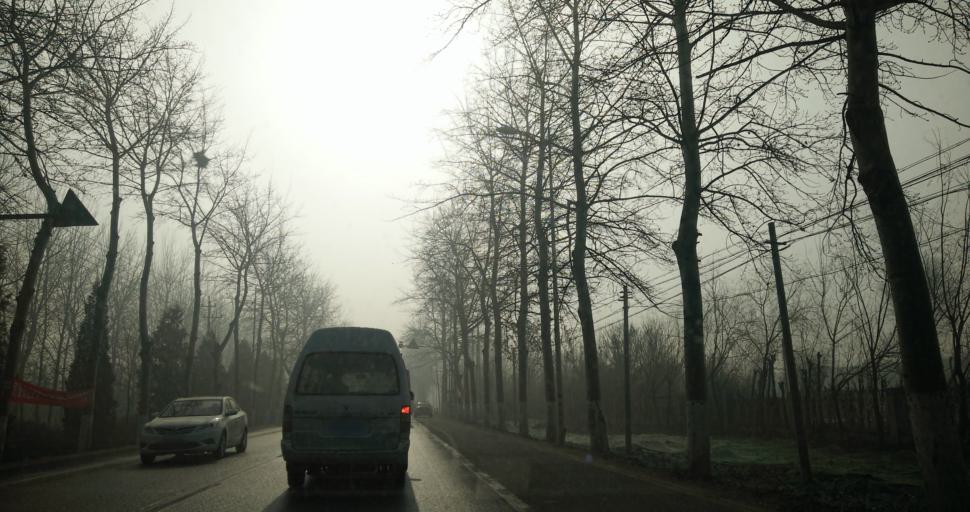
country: CN
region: Beijing
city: Yinghai
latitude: 39.7480
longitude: 116.4470
